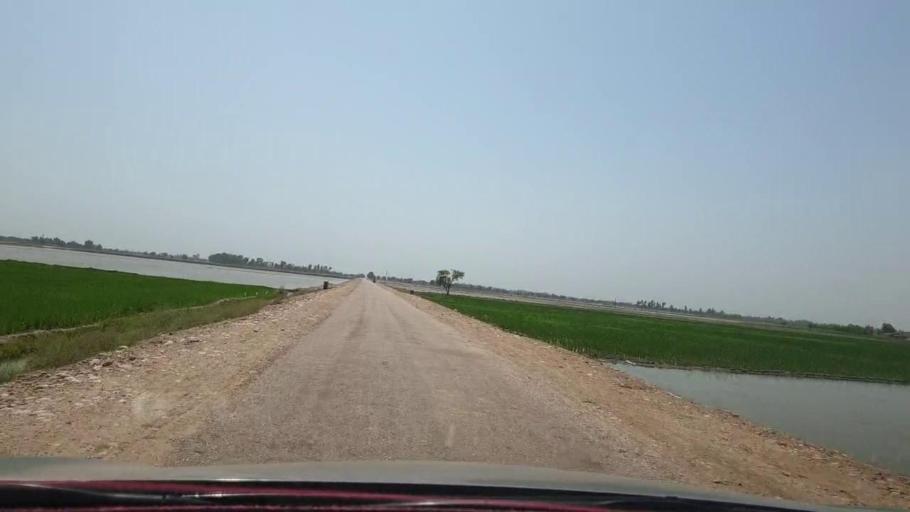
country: PK
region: Sindh
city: Warah
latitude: 27.5495
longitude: 67.7952
